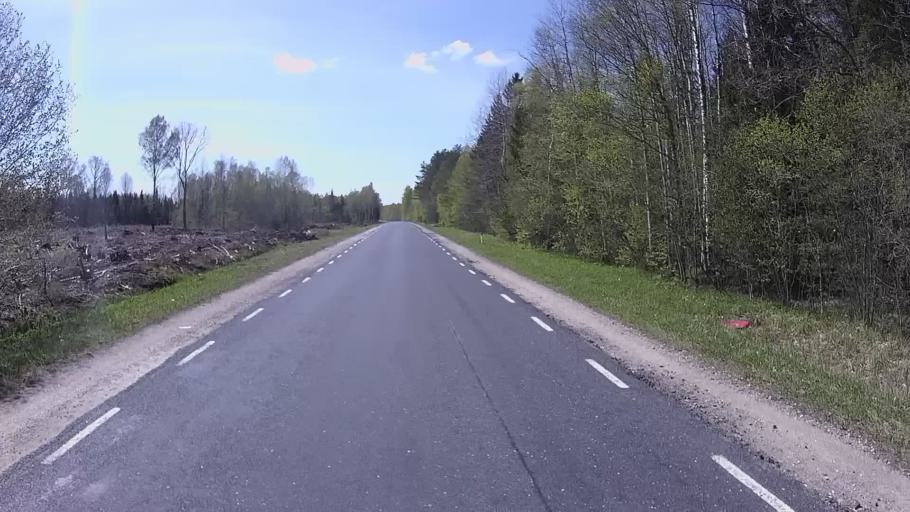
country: EE
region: Laeaene
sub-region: Ridala Parish
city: Uuemoisa
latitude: 59.0268
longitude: 23.8108
